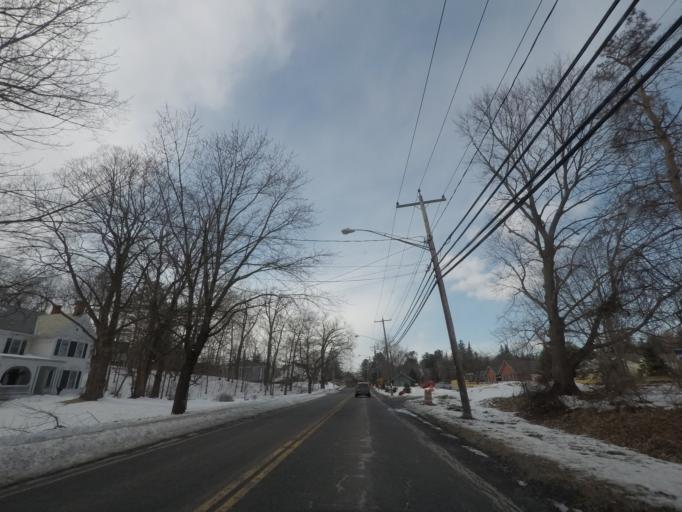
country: US
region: New York
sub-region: Albany County
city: Delmar
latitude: 42.6288
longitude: -73.8619
